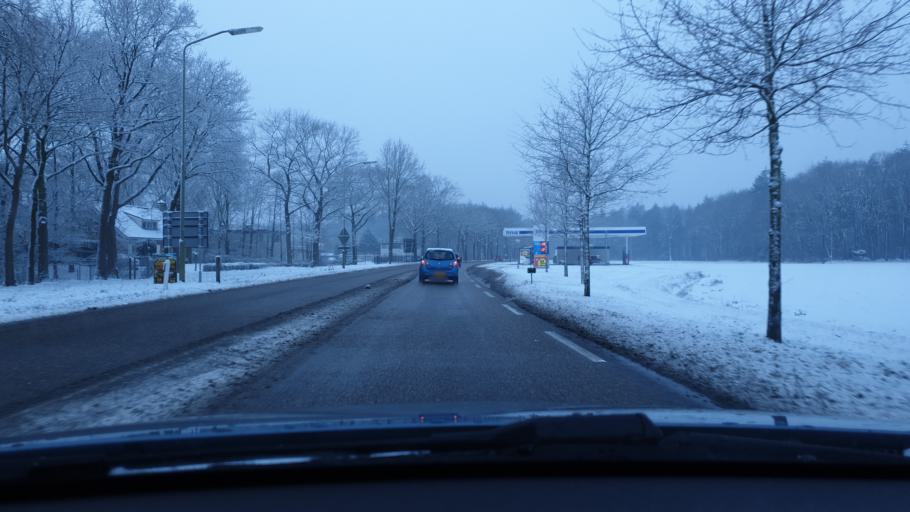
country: NL
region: North Brabant
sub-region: Gemeente Landerd
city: Zeeland
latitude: 51.6875
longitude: 5.6603
